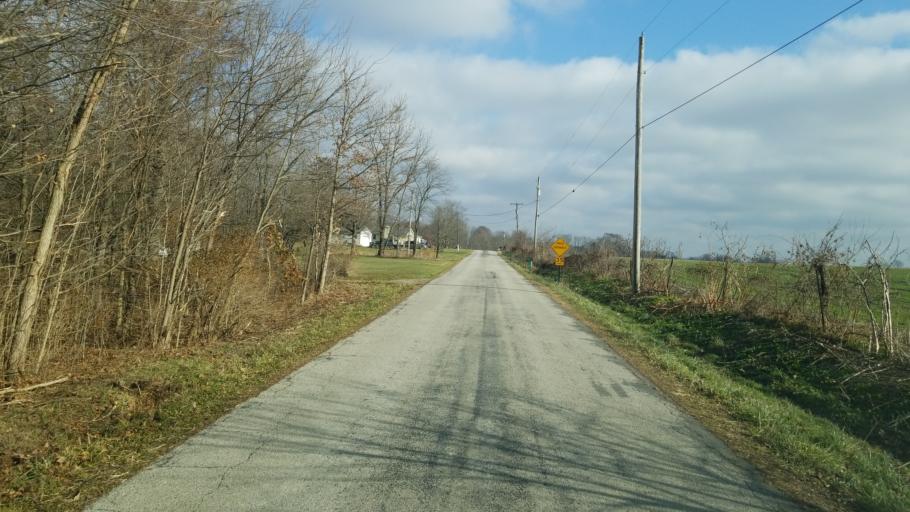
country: US
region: Ohio
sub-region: Richland County
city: Lincoln Heights
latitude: 40.8148
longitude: -82.4471
